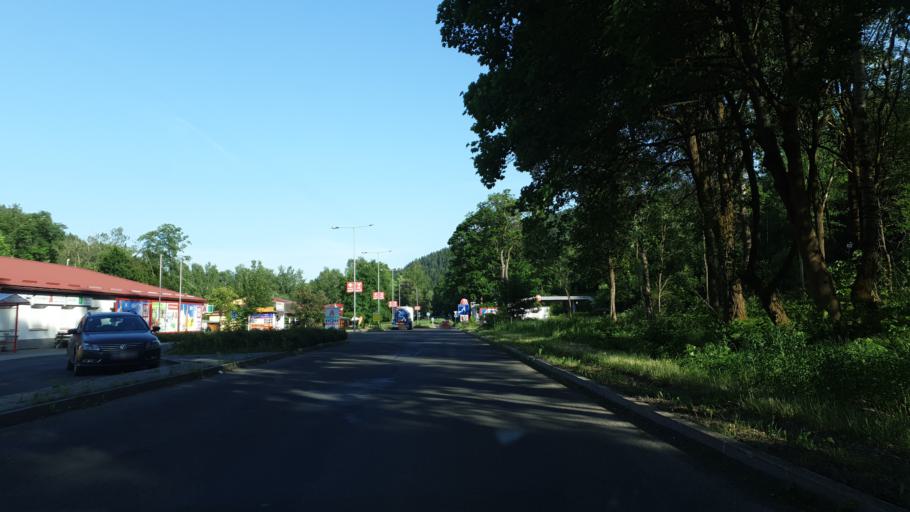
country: DE
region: Saxony
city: Klingenthal
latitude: 50.3535
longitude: 12.4699
